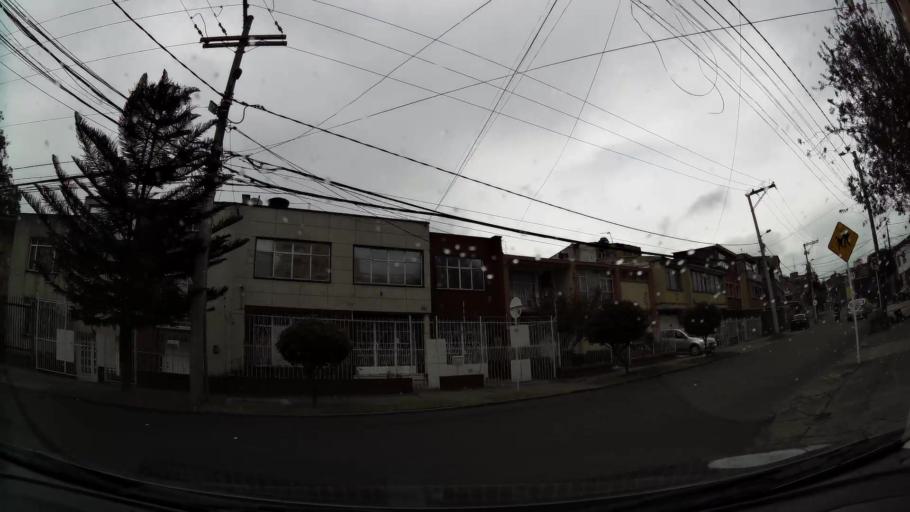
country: CO
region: Bogota D.C.
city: Bogota
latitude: 4.6268
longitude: -74.0794
